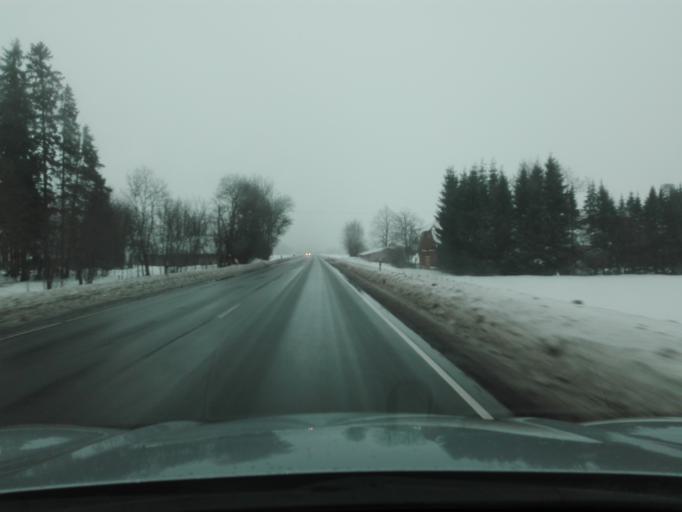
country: EE
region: Raplamaa
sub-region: Kohila vald
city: Kohila
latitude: 59.2032
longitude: 24.7819
